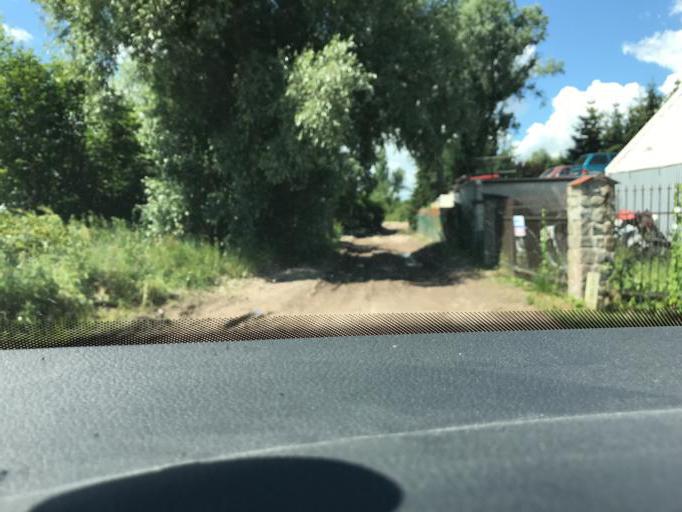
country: PL
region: Pomeranian Voivodeship
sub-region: Gdansk
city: Gdansk
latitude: 54.3196
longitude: 18.7473
